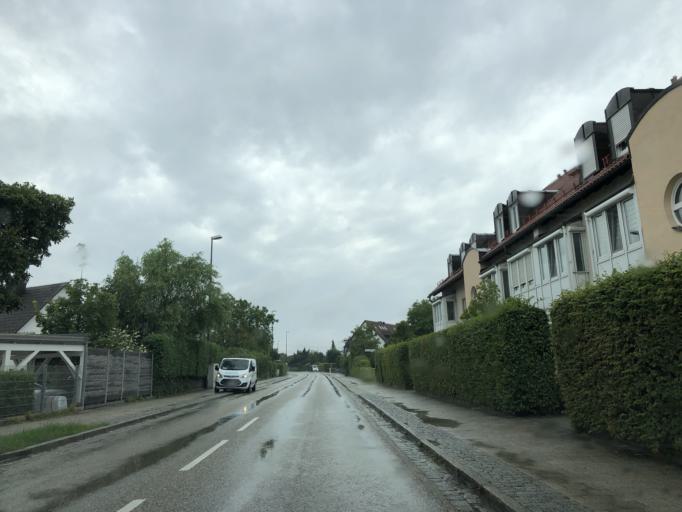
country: DE
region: Bavaria
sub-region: Upper Bavaria
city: Eching
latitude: 48.2941
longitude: 11.6186
